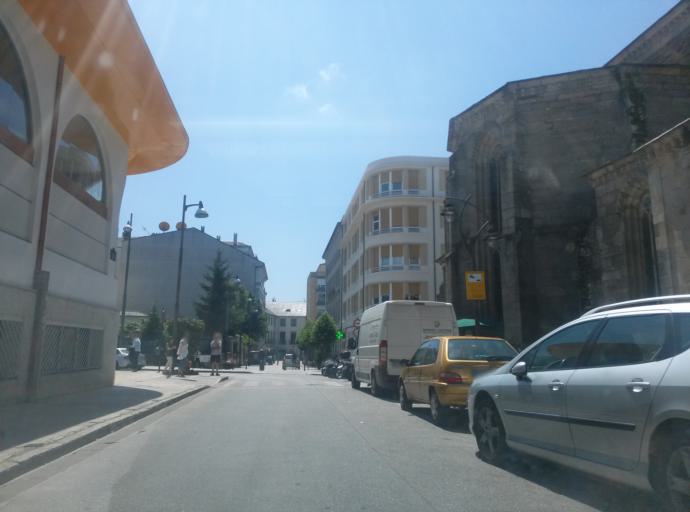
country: ES
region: Galicia
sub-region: Provincia de Lugo
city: Lugo
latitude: 43.0118
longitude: -7.5582
